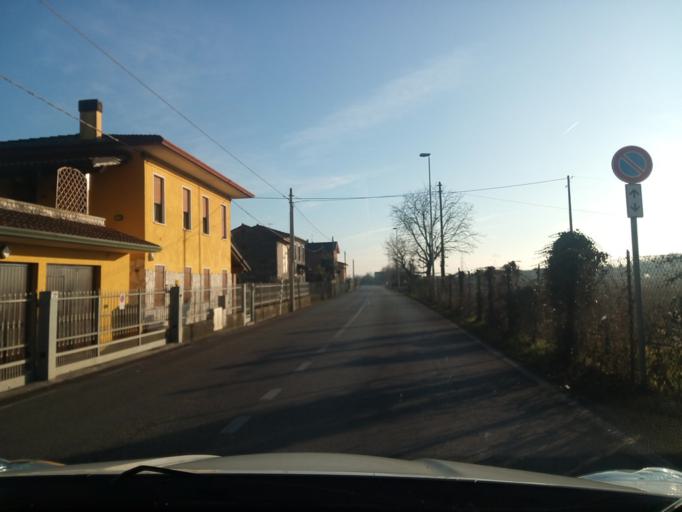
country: IT
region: Veneto
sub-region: Provincia di Vicenza
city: Dueville
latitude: 45.6409
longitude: 11.5641
